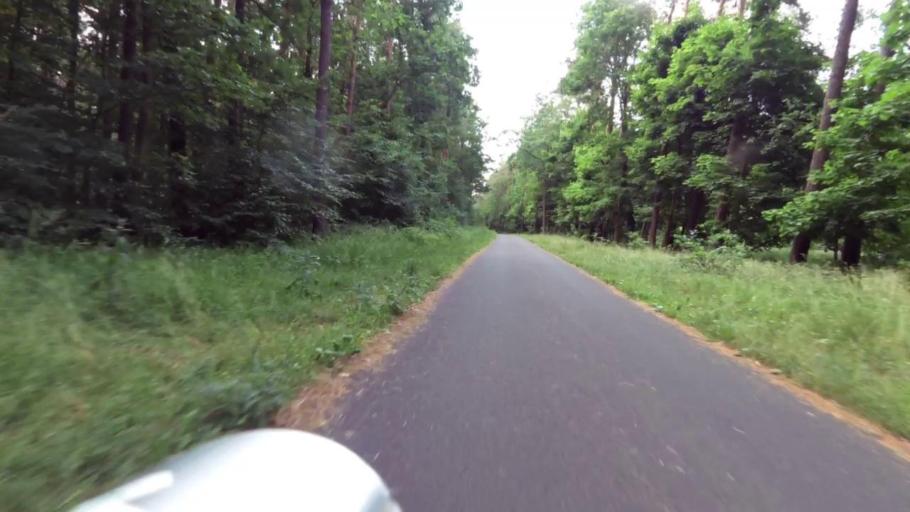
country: PL
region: Kujawsko-Pomorskie
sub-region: Torun
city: Torun
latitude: 53.0622
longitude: 18.5554
